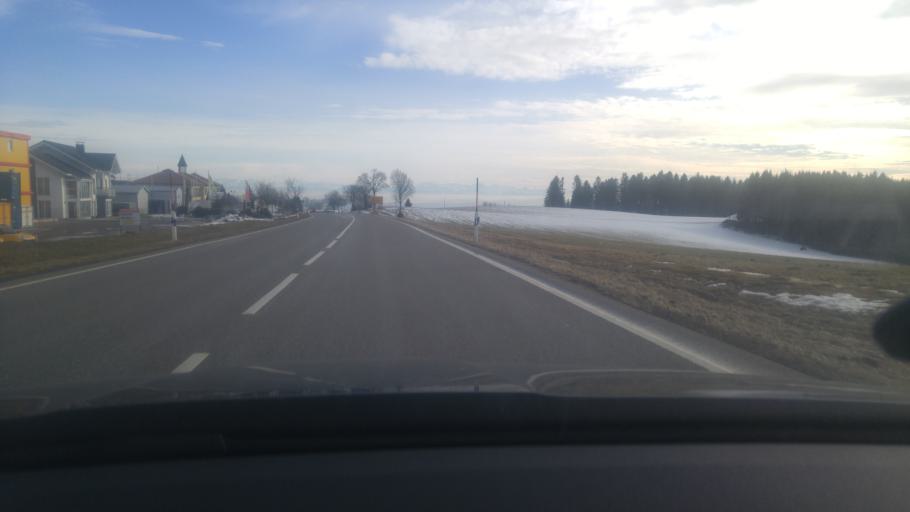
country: DE
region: Baden-Wuerttemberg
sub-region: Freiburg Region
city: Hochenschwand
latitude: 47.7062
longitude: 8.1434
